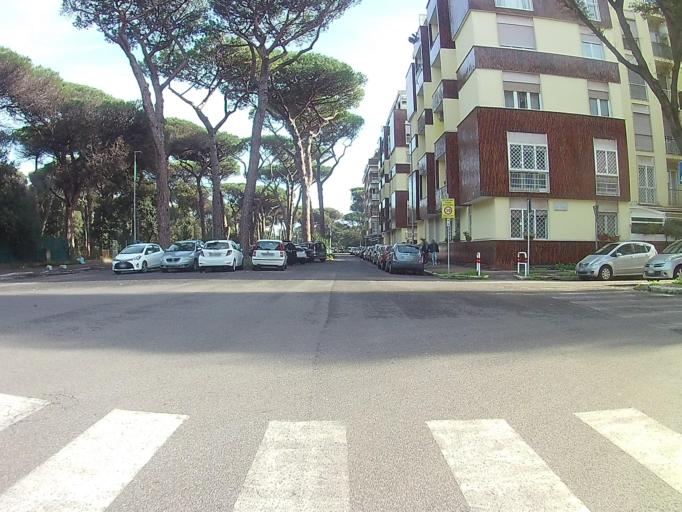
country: IT
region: Latium
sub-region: Citta metropolitana di Roma Capitale
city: Lido di Ostia
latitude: 41.7343
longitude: 12.3009
